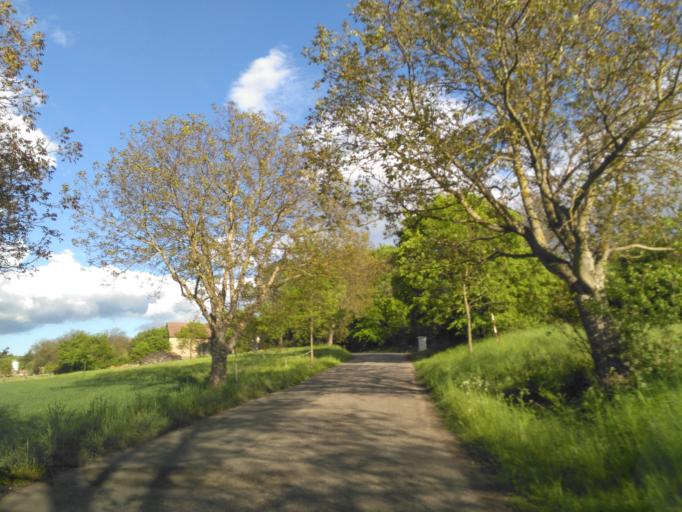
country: CZ
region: Central Bohemia
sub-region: Okres Beroun
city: Kraluv Dvur
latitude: 49.9220
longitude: 14.0597
